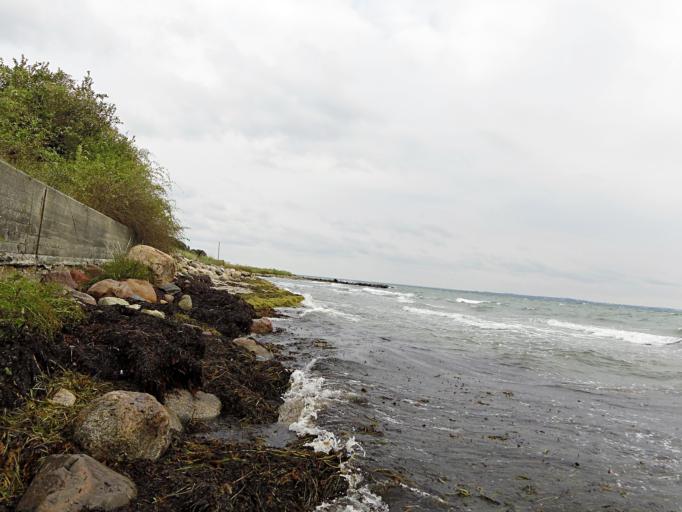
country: DK
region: Capital Region
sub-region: Rudersdal Kommune
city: Trorod
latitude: 55.8325
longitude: 12.5743
